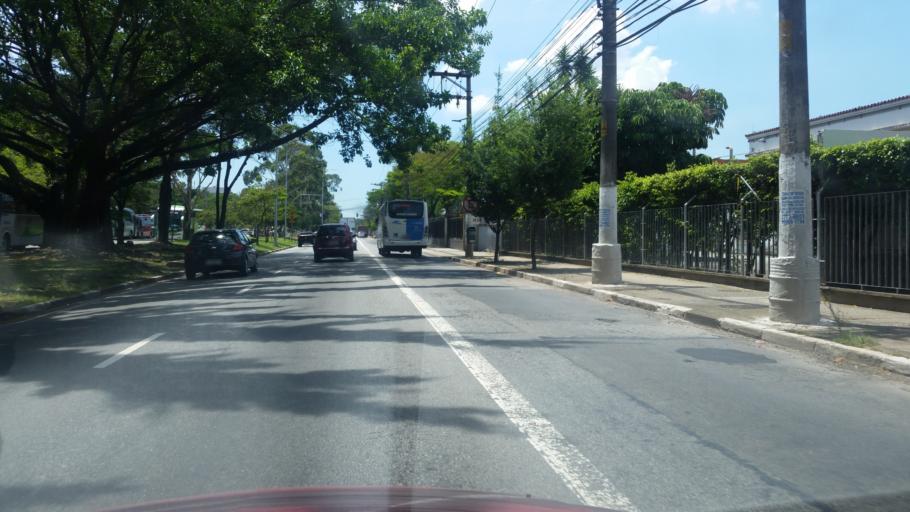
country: BR
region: Sao Paulo
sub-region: Diadema
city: Diadema
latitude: -23.6723
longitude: -46.7024
